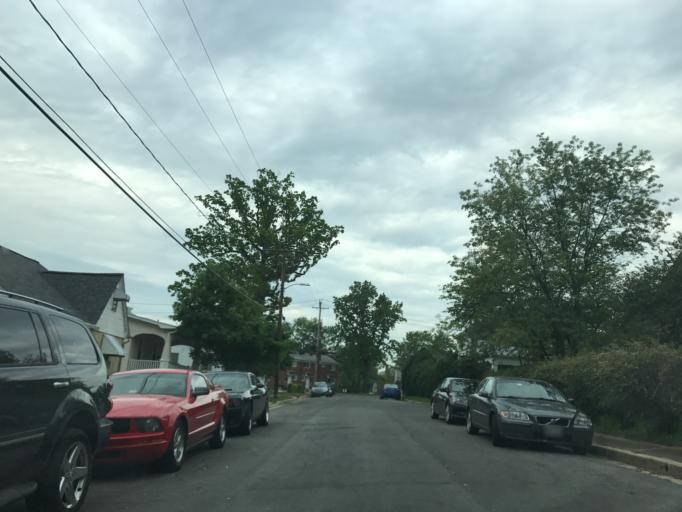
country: US
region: Maryland
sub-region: Baltimore County
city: Parkville
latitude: 39.3603
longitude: -76.5706
